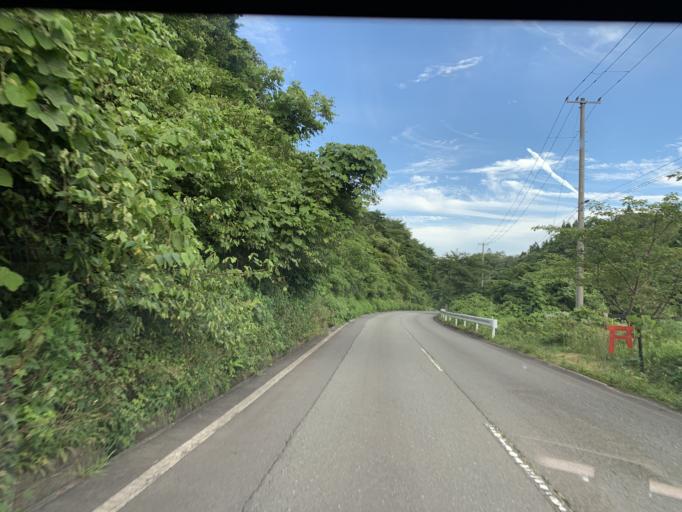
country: JP
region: Iwate
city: Ichinoseki
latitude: 38.8970
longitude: 141.0053
